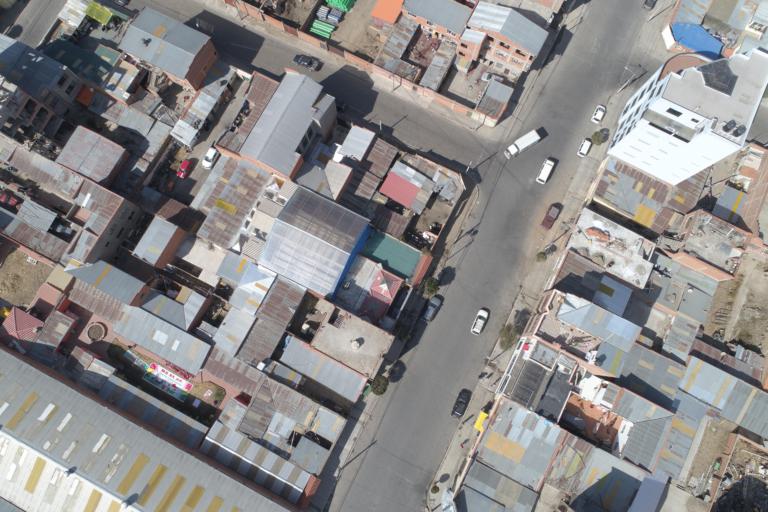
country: BO
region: La Paz
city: La Paz
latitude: -16.5291
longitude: -68.1478
